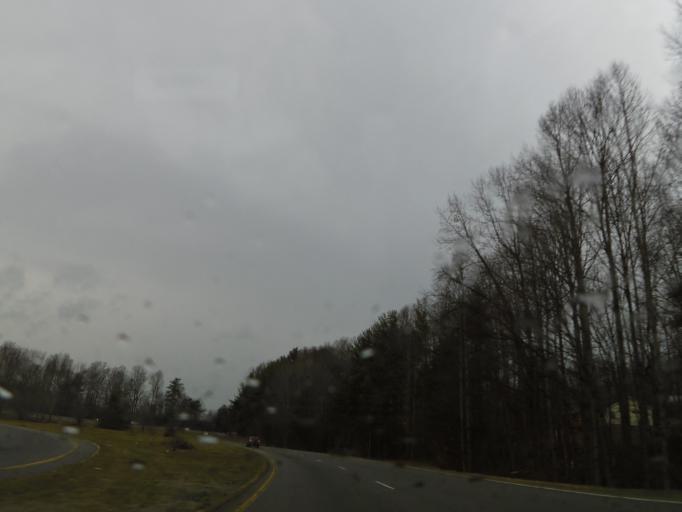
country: US
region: North Carolina
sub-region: Henderson County
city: East Flat Rock
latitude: 35.2856
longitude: -82.3991
